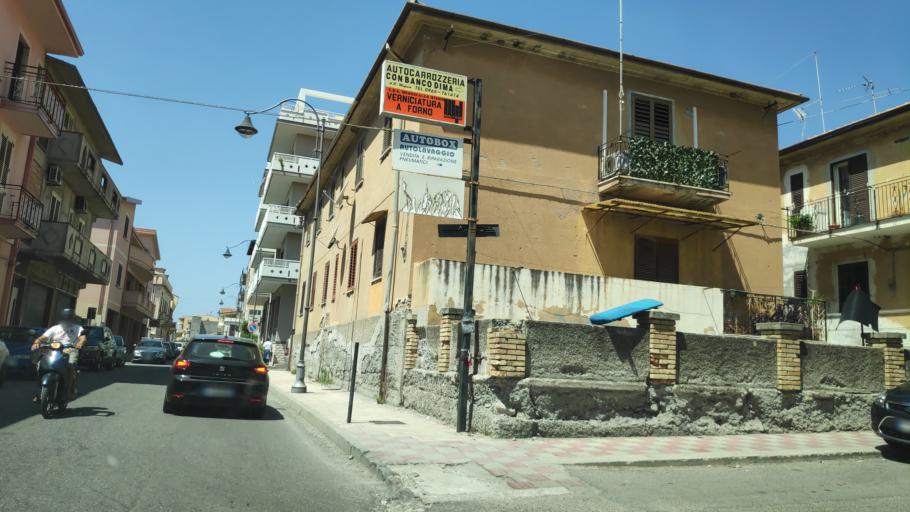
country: IT
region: Calabria
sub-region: Provincia di Reggio Calabria
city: Bova Marina
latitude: 37.9304
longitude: 15.9178
